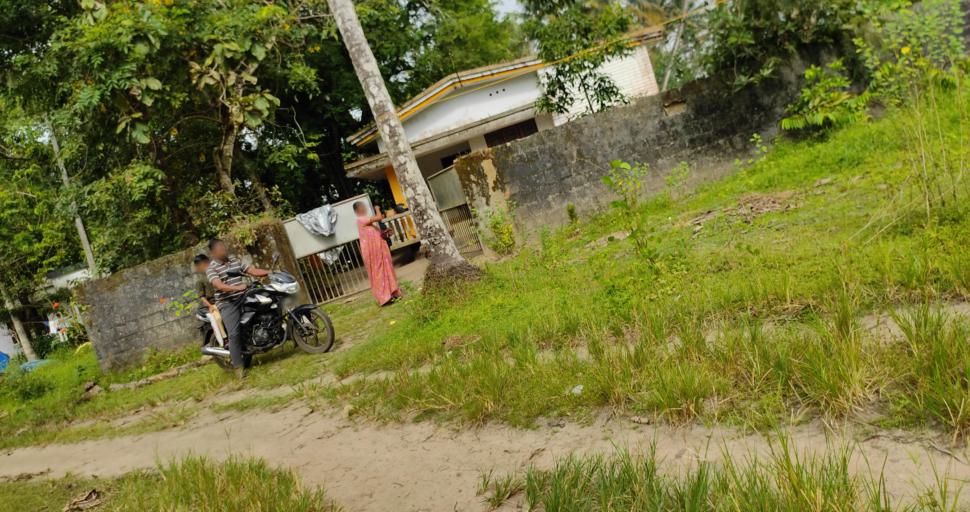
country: IN
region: Kerala
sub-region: Alappuzha
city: Vayalar
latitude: 9.6737
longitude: 76.2926
